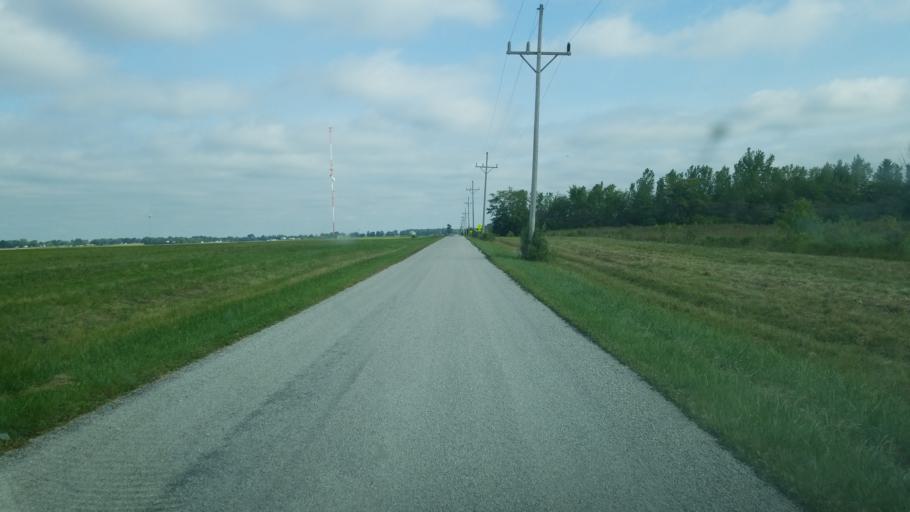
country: US
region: Ohio
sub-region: Marion County
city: Marion
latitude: 40.5914
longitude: -83.2033
